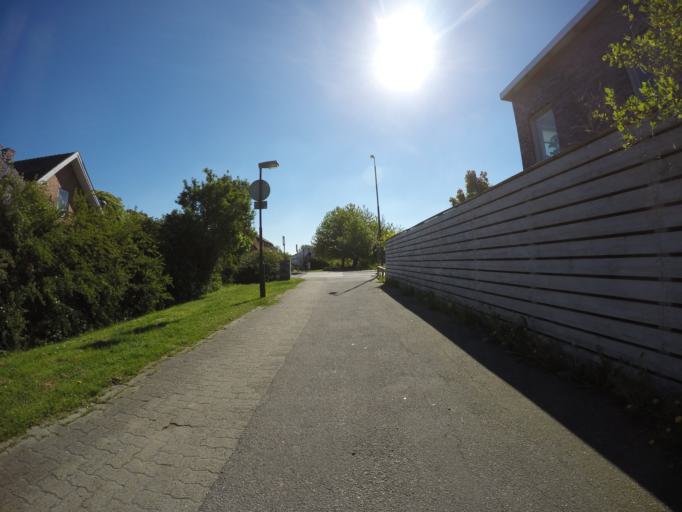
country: SE
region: Skane
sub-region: Burlovs Kommun
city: Arloev
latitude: 55.5895
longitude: 13.0609
